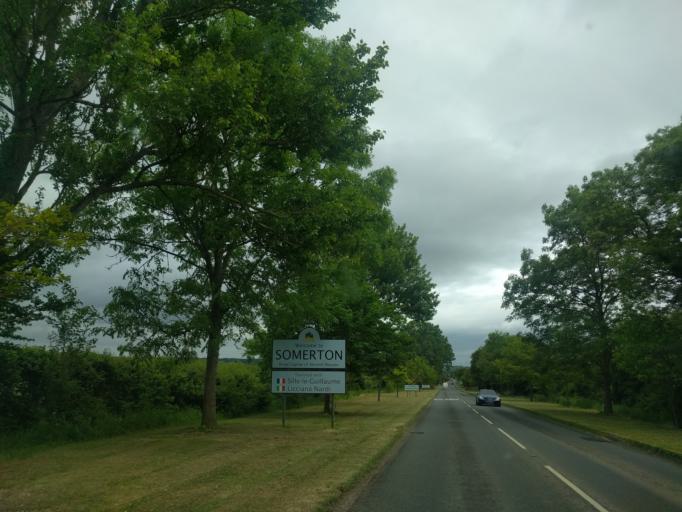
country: GB
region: England
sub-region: Somerset
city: Langport
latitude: 51.0524
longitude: -2.7571
